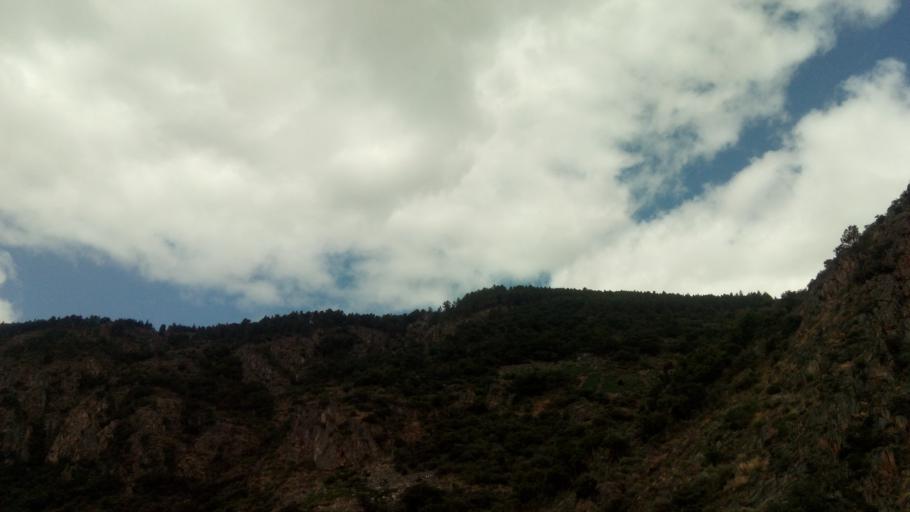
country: ES
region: Galicia
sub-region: Provincia de Lugo
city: Lobios
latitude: 42.4044
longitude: -7.5721
